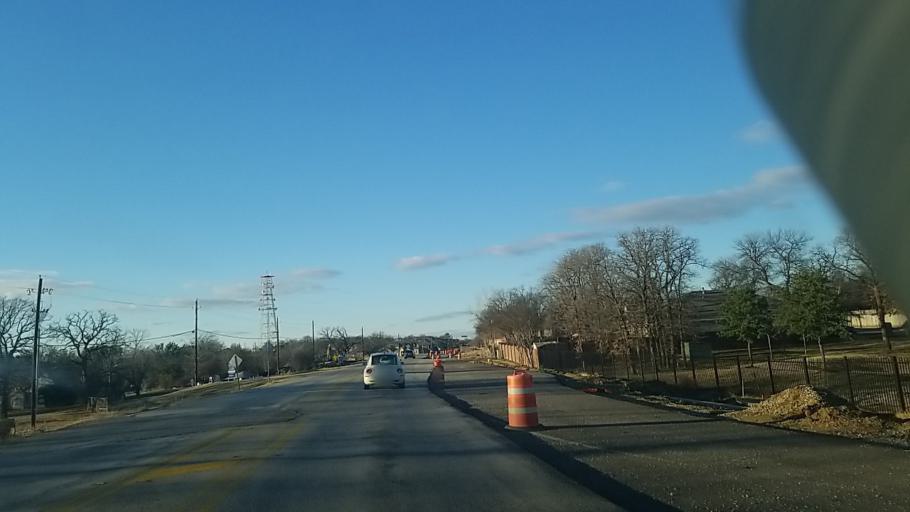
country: US
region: Texas
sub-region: Denton County
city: Corinth
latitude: 33.1631
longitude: -97.1077
